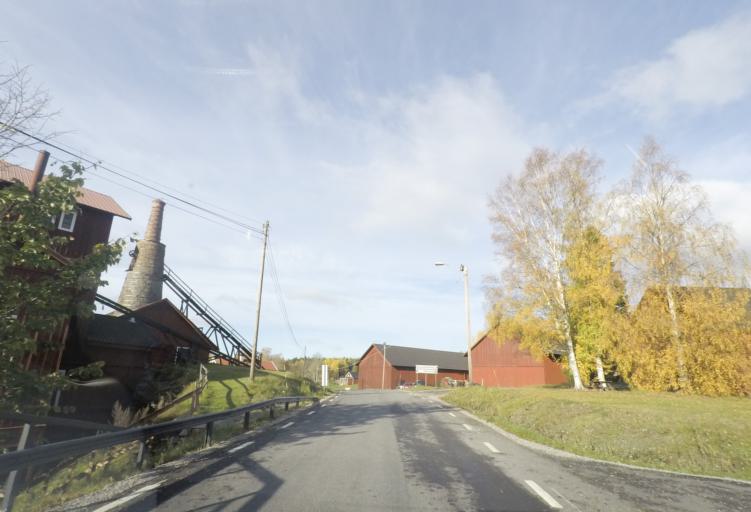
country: SE
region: OErebro
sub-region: Lindesbergs Kommun
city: Stora
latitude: 59.8030
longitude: 15.1670
